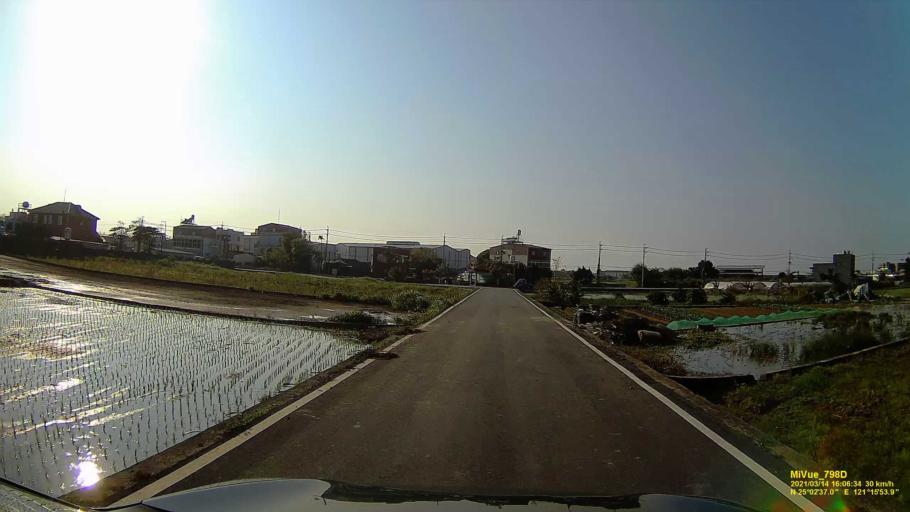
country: TW
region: Taiwan
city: Taoyuan City
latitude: 25.0437
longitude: 121.2648
